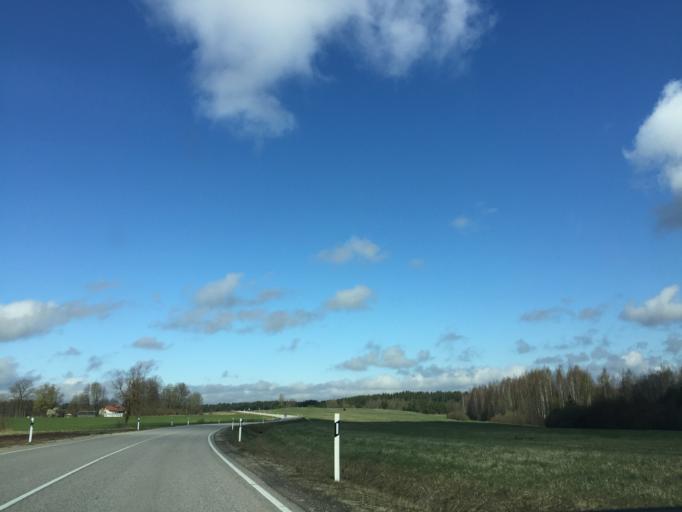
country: LV
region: Apes Novads
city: Ape
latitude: 57.5301
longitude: 26.7298
